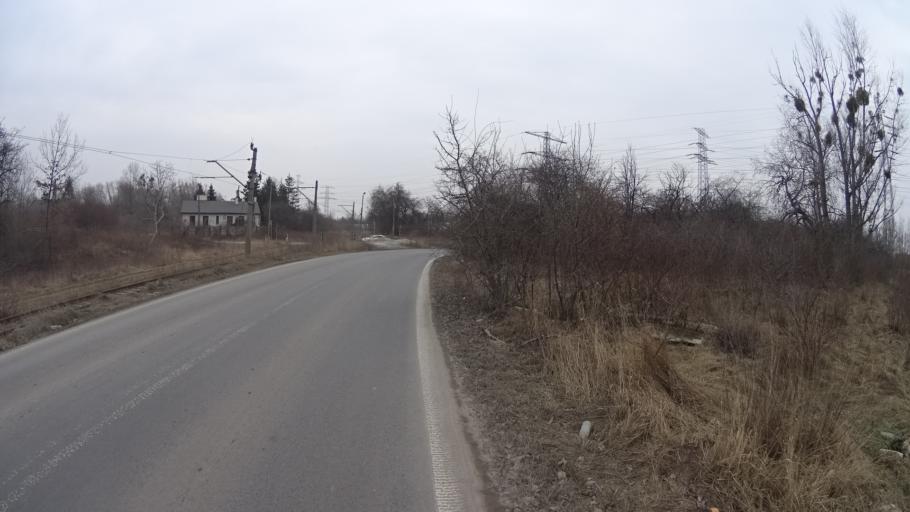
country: PL
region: Masovian Voivodeship
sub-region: Warszawa
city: Ochota
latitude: 52.2196
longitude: 20.9457
